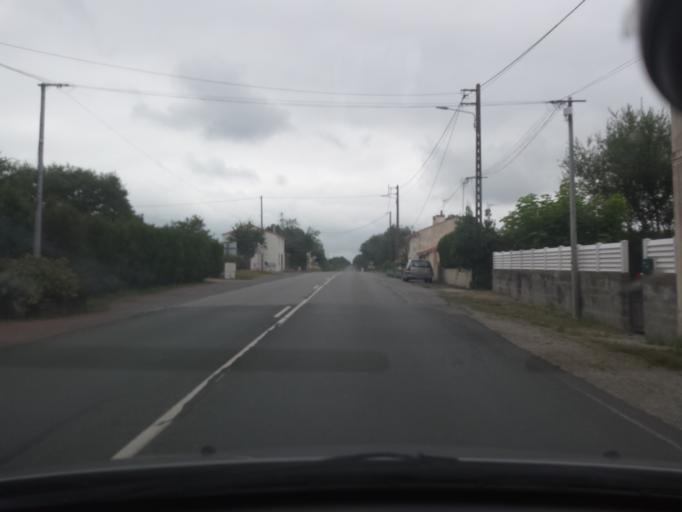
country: FR
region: Pays de la Loire
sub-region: Departement de la Vendee
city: Saint-Florent-des-Bois
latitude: 46.5999
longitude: -1.3269
